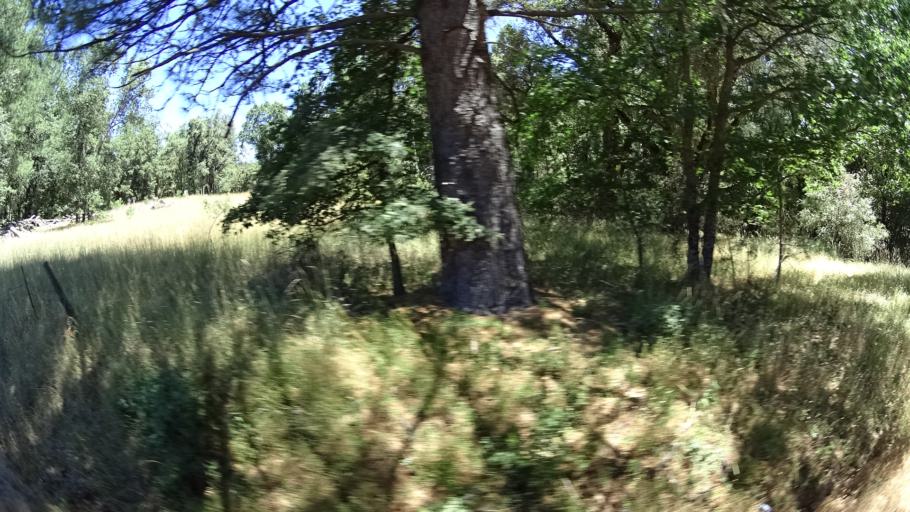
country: US
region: California
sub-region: Amador County
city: Pioneer
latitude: 38.3485
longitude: -120.5586
